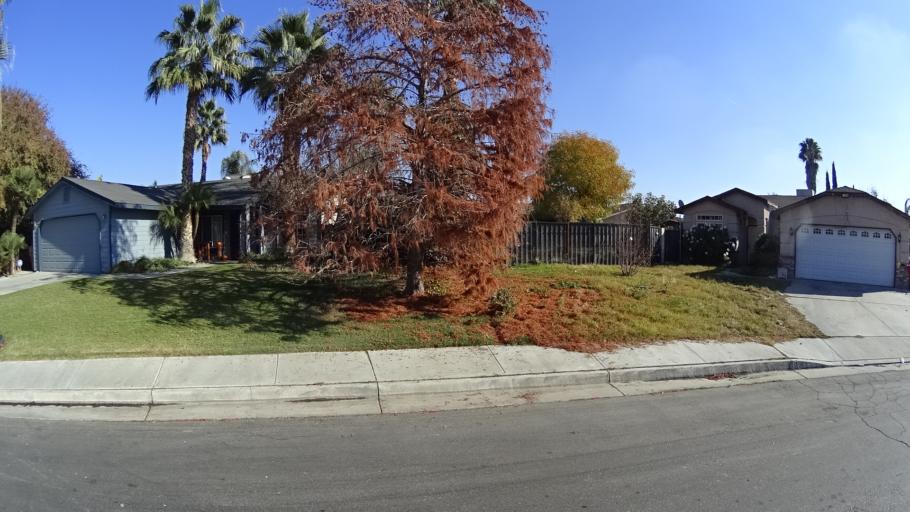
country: US
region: California
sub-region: Kern County
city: Greenfield
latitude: 35.2895
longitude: -119.0487
